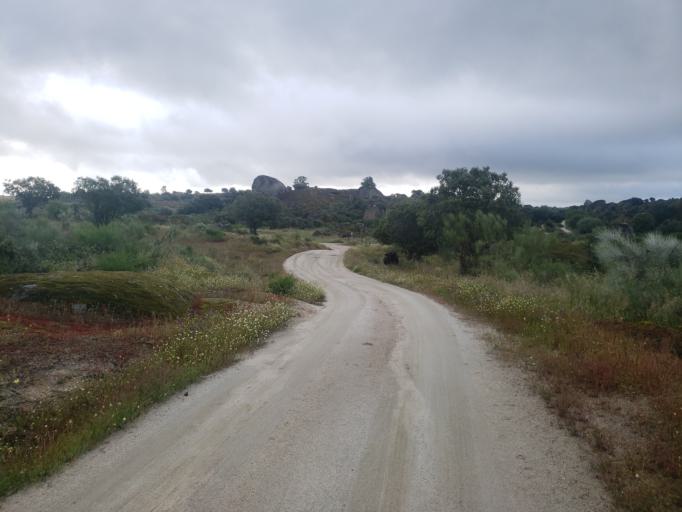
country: ES
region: Extremadura
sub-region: Provincia de Caceres
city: Malpartida de Caceres
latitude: 39.4266
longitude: -6.4946
